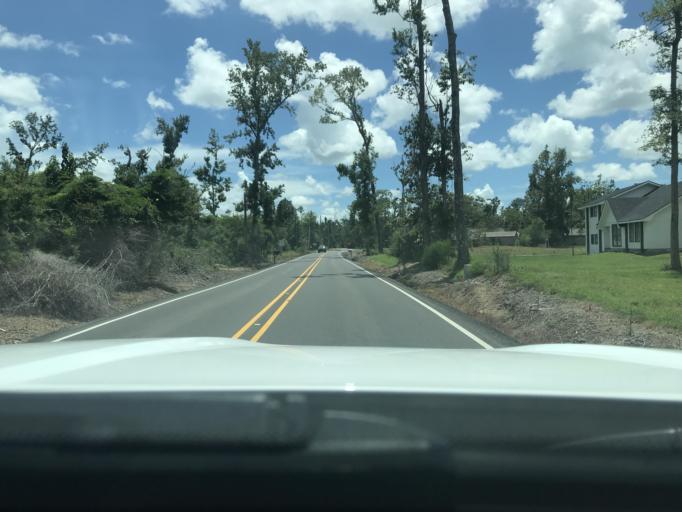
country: US
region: Louisiana
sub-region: Calcasieu Parish
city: Moss Bluff
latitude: 30.3098
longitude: -93.1829
